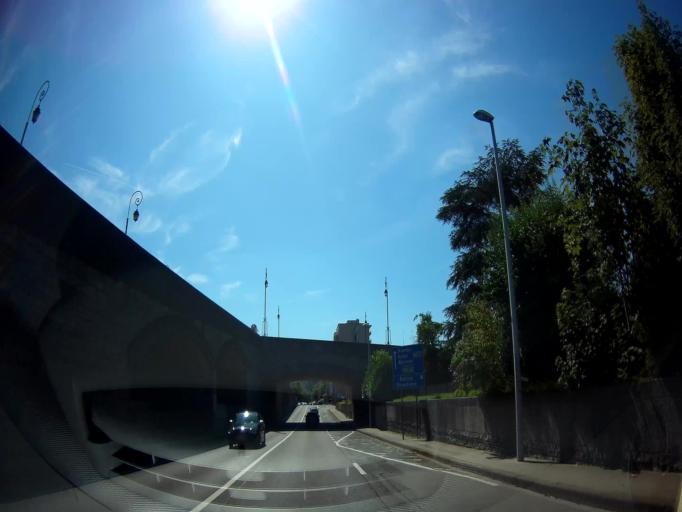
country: BE
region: Wallonia
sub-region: Province de Liege
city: Huy
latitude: 50.5259
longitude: 5.2395
